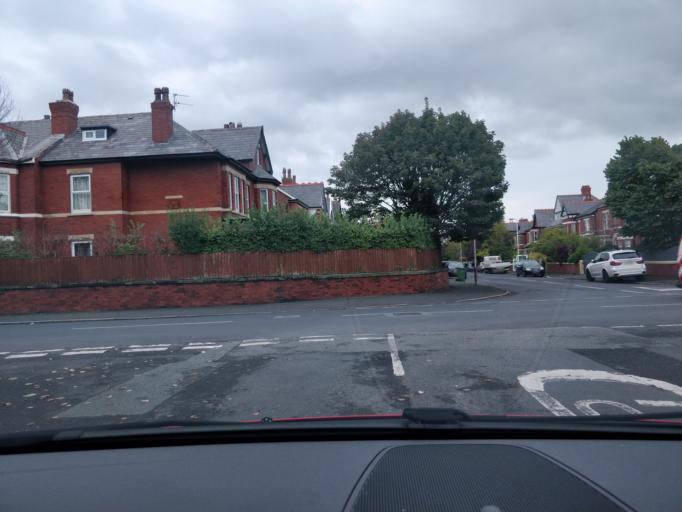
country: GB
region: England
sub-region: Sefton
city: Southport
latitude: 53.6374
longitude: -2.9916
